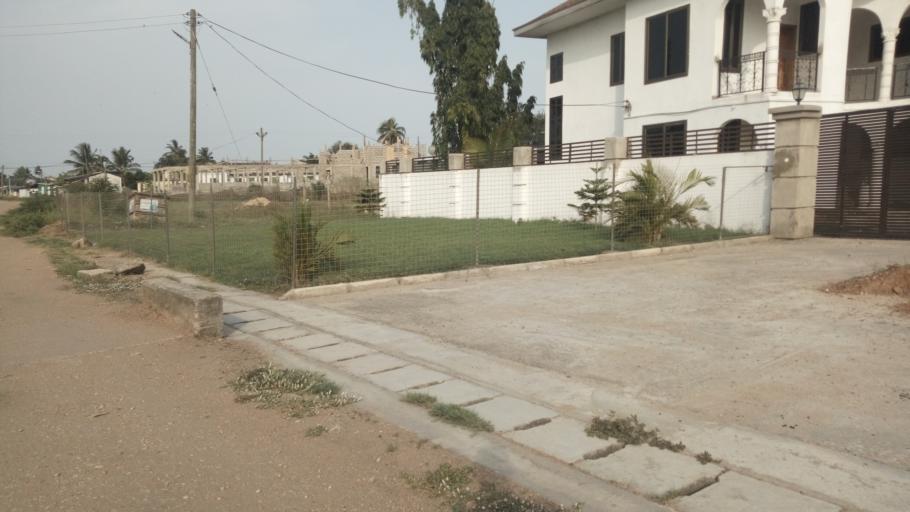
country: GH
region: Central
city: Winneba
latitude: 5.3506
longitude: -0.6335
